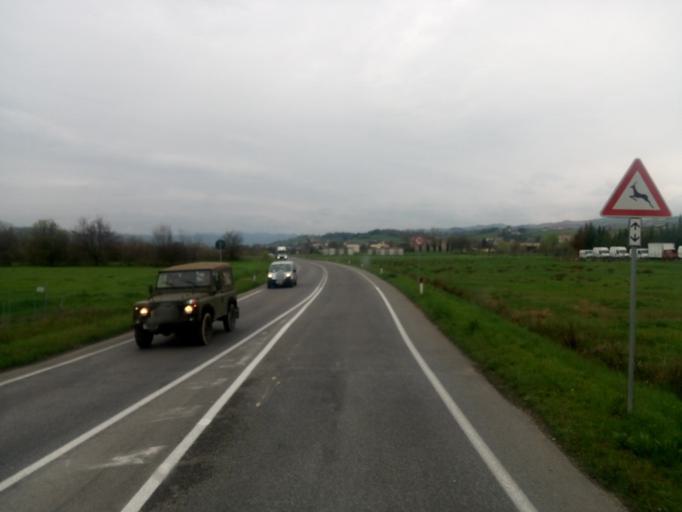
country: IT
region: Emilia-Romagna
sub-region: Forli-Cesena
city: Meldola
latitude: 44.1425
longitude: 12.0686
